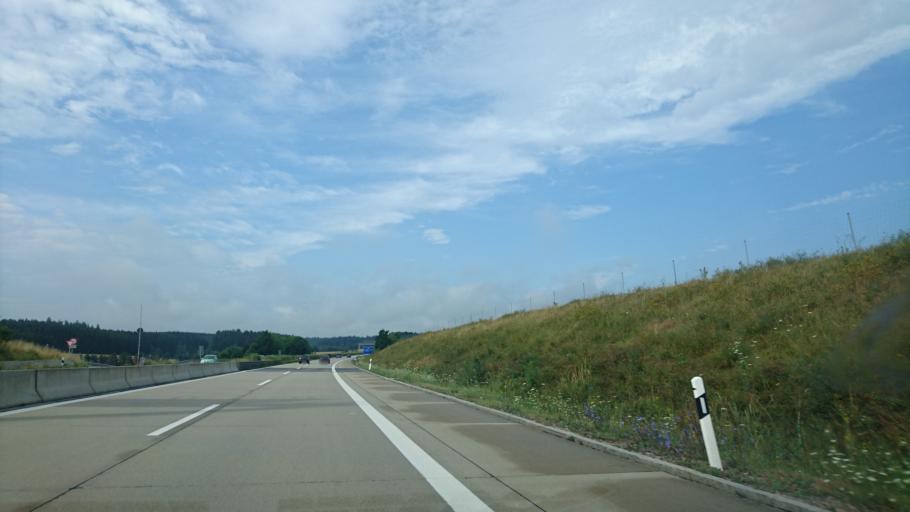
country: DE
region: Bavaria
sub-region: Lower Bavaria
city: Bad Abbach
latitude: 48.8873
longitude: 12.0716
